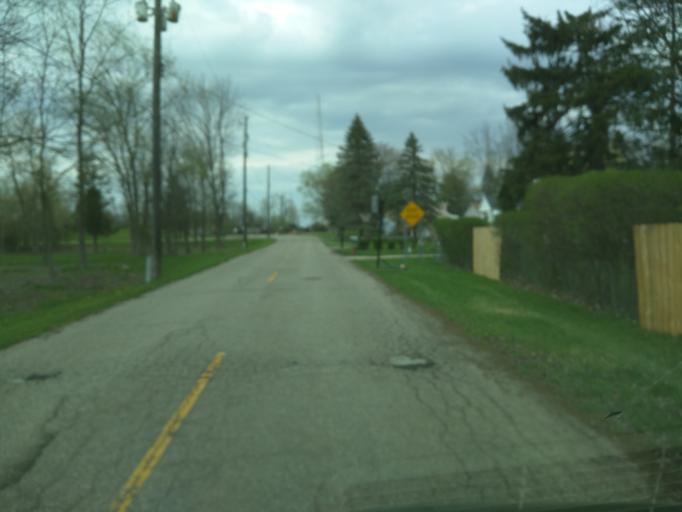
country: US
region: Michigan
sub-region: Eaton County
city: Waverly
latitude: 42.7000
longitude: -84.6227
